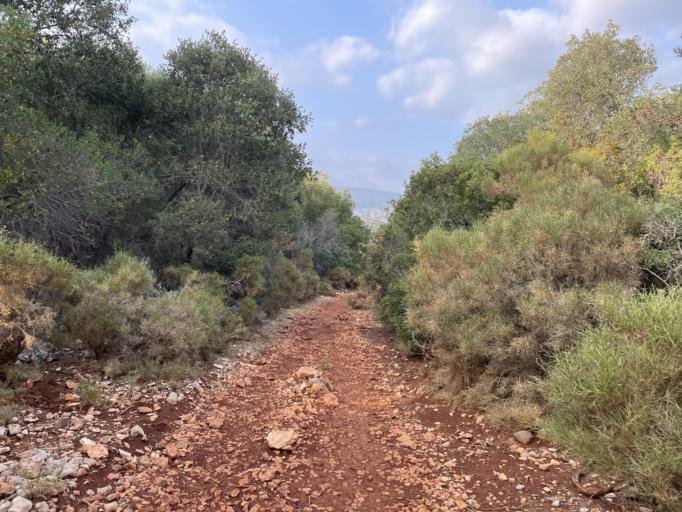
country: TR
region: Antalya
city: Kas
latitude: 36.1638
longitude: 29.6541
